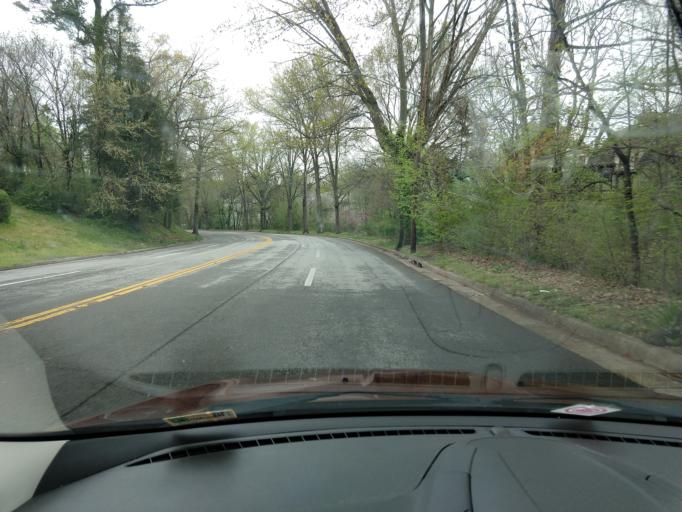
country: US
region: Virginia
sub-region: City of Danville
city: Danville
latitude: 36.5726
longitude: -79.4312
